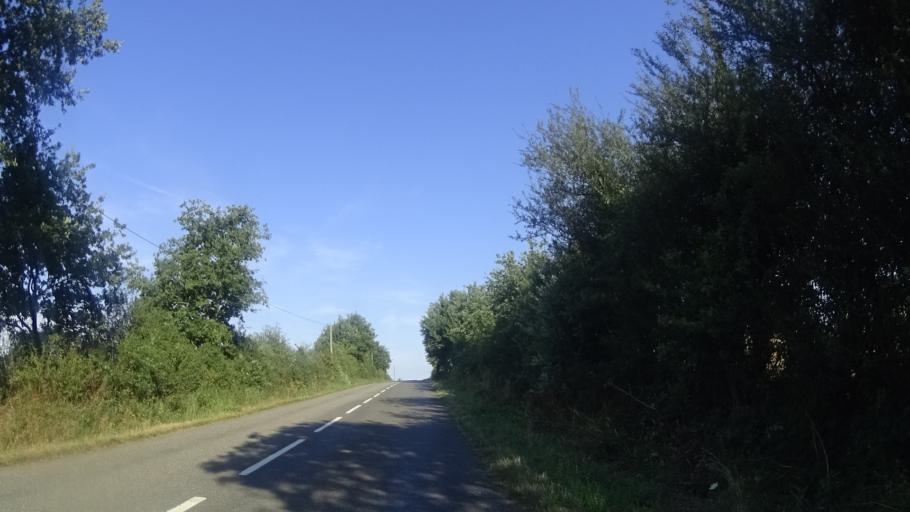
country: FR
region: Pays de la Loire
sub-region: Departement de la Loire-Atlantique
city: Joue-sur-Erdre
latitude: 47.4837
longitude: -1.3894
